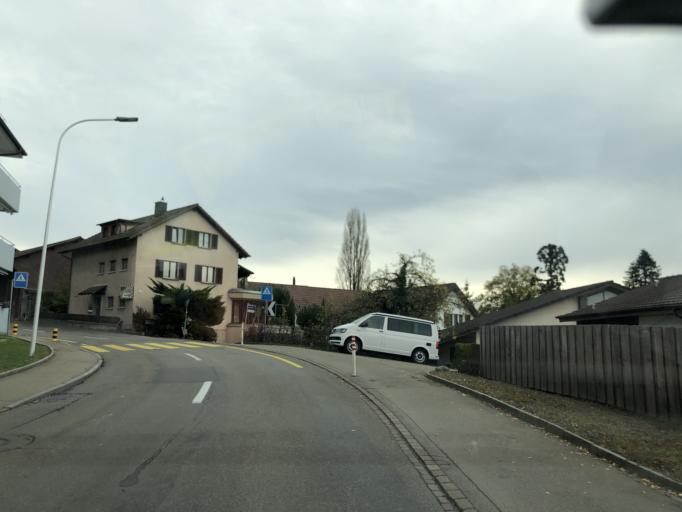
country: CH
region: Aargau
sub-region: Bezirk Baden
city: Obersiggenthal
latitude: 47.4870
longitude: 8.3001
